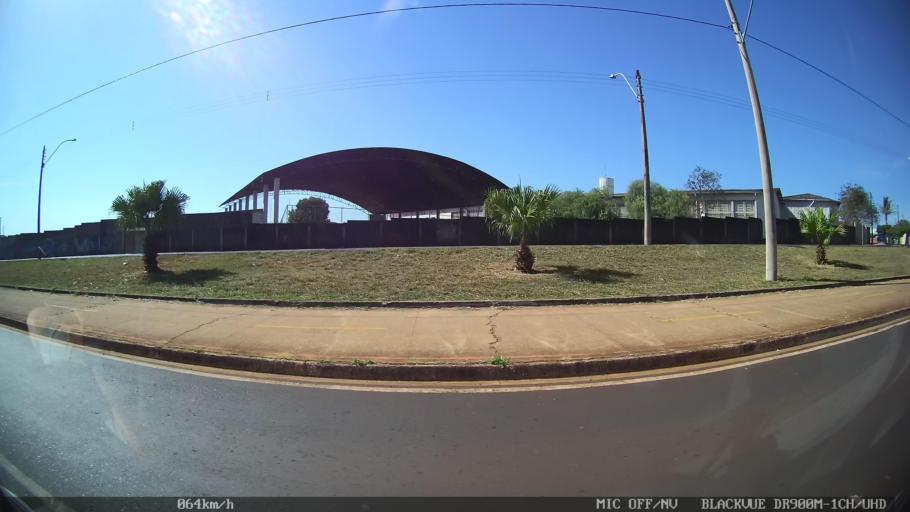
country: BR
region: Sao Paulo
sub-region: Batatais
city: Batatais
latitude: -20.9118
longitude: -47.5830
